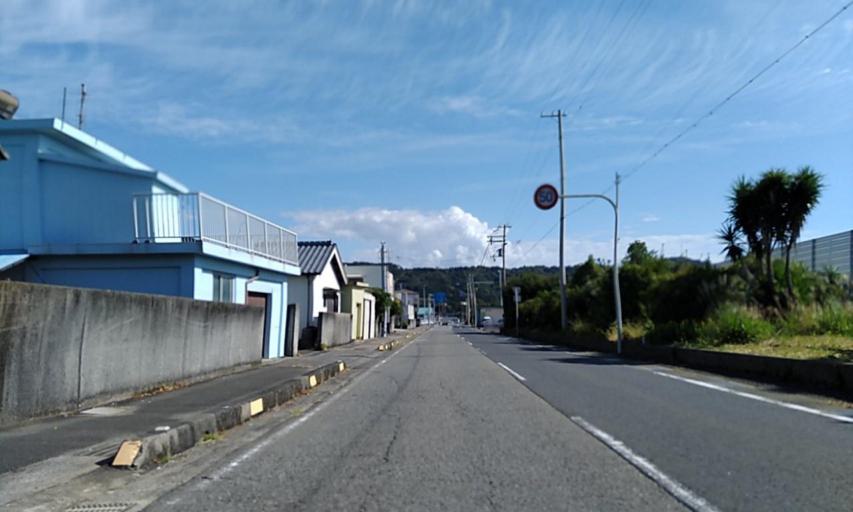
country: JP
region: Wakayama
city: Gobo
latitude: 33.8007
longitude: 135.2336
